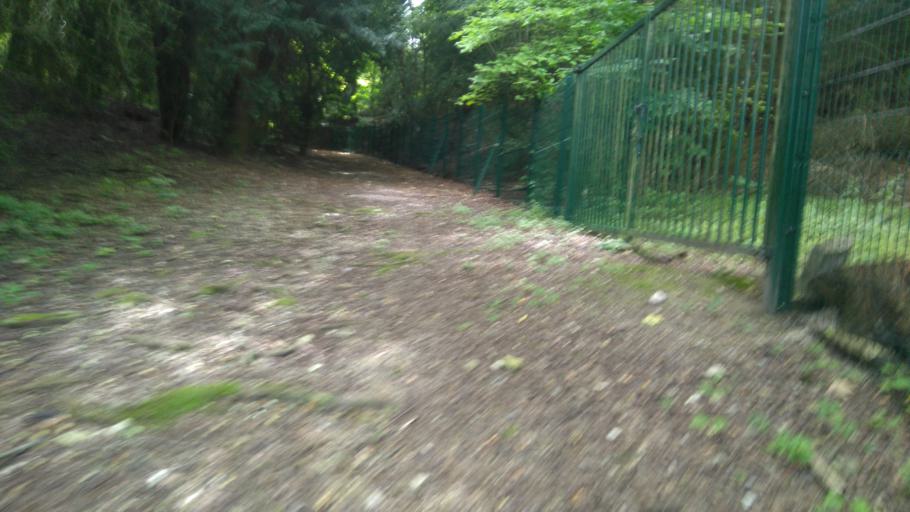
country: FR
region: Picardie
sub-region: Departement de l'Oise
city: Saint-Maximin
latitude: 49.2355
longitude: 2.4494
